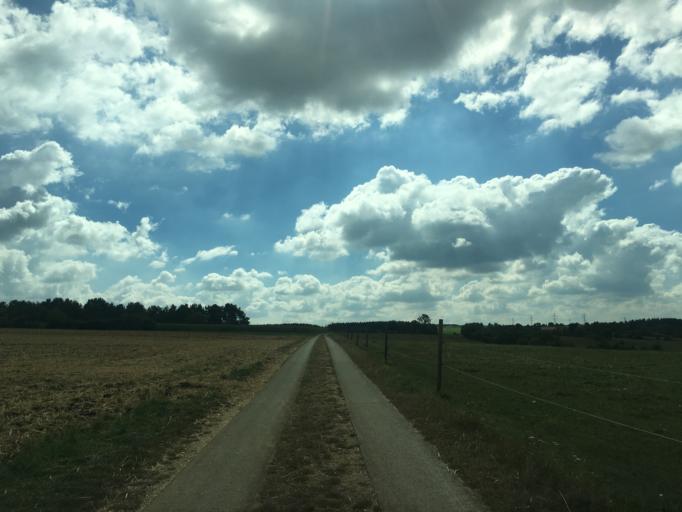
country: DE
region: Baden-Wuerttemberg
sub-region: Tuebingen Region
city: Hayingen
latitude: 48.2752
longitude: 9.4911
